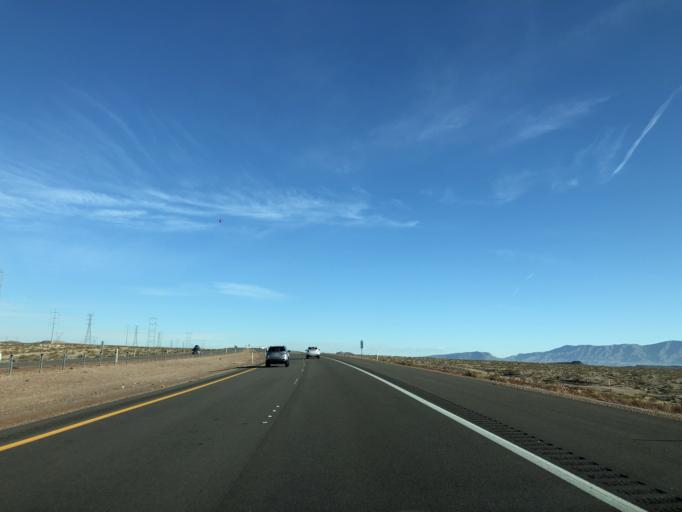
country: US
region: Nevada
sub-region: Clark County
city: Boulder City
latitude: 35.9426
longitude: -114.8116
